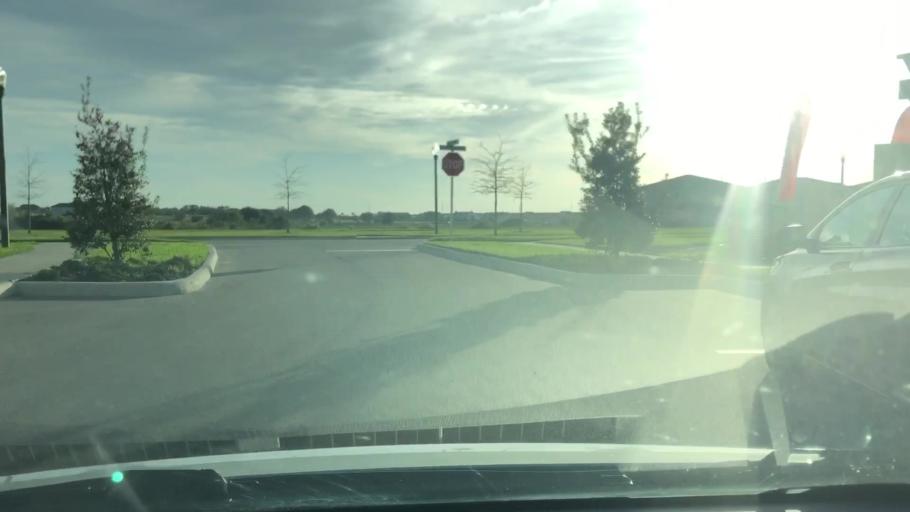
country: US
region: Florida
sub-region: Polk County
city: Citrus Ridge
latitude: 28.4274
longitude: -81.6200
